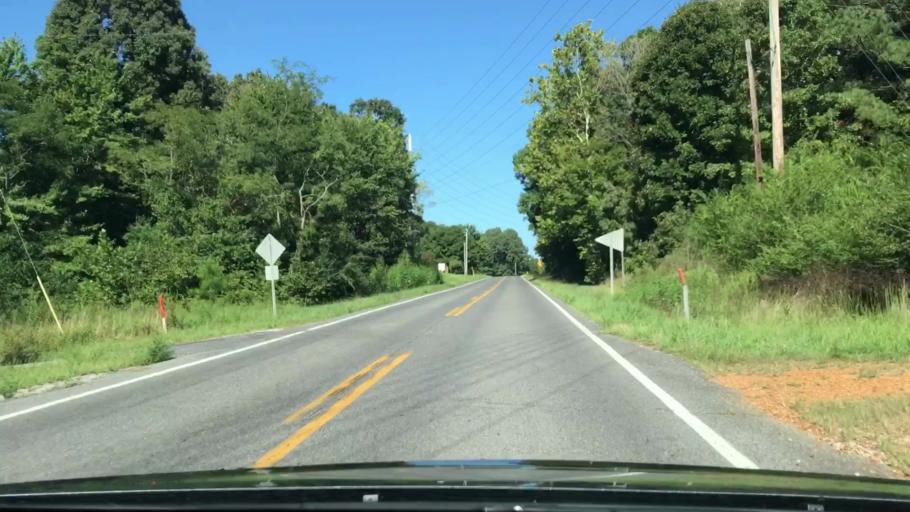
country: US
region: Kentucky
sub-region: Graves County
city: Mayfield
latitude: 36.7749
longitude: -88.4868
